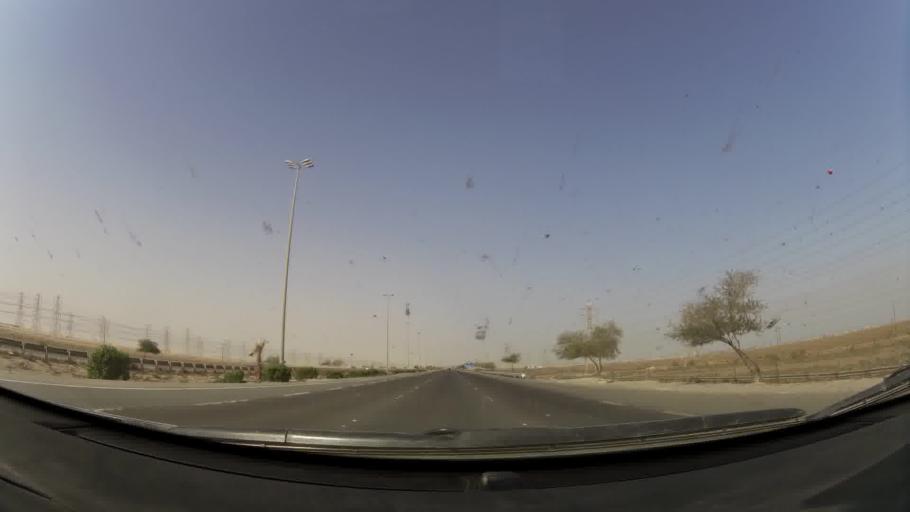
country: KW
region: Al Ahmadi
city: Al Fahahil
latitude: 28.8452
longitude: 48.2475
